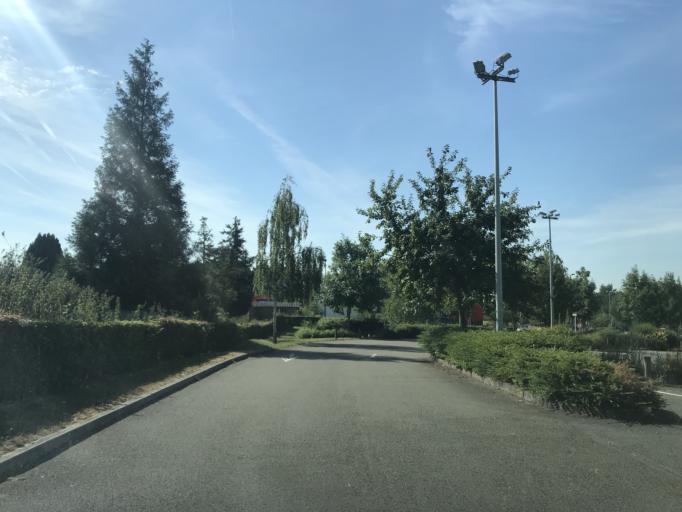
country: FR
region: Haute-Normandie
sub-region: Departement de la Seine-Maritime
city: Roumare
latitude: 49.5279
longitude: 0.9666
